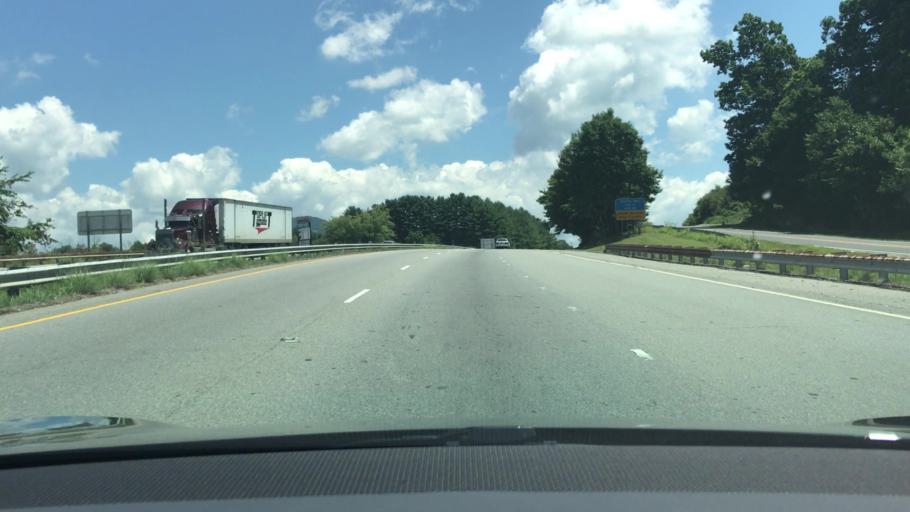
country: US
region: North Carolina
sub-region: Haywood County
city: Lake Junaluska
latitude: 35.5247
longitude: -82.9553
